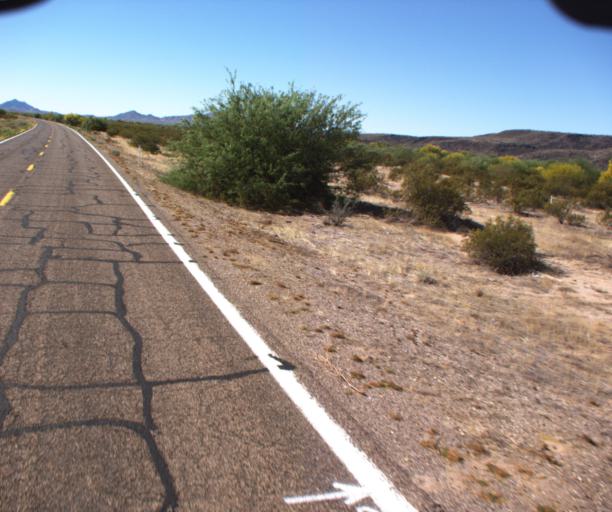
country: US
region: Arizona
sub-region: Pima County
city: Ajo
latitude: 32.4912
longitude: -112.8816
